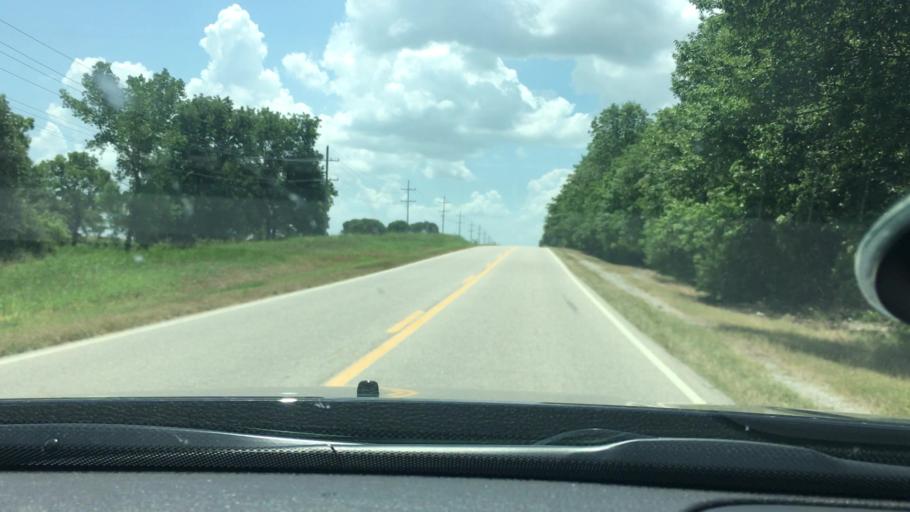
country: US
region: Oklahoma
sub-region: Pontotoc County
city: Ada
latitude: 34.6768
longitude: -96.6349
